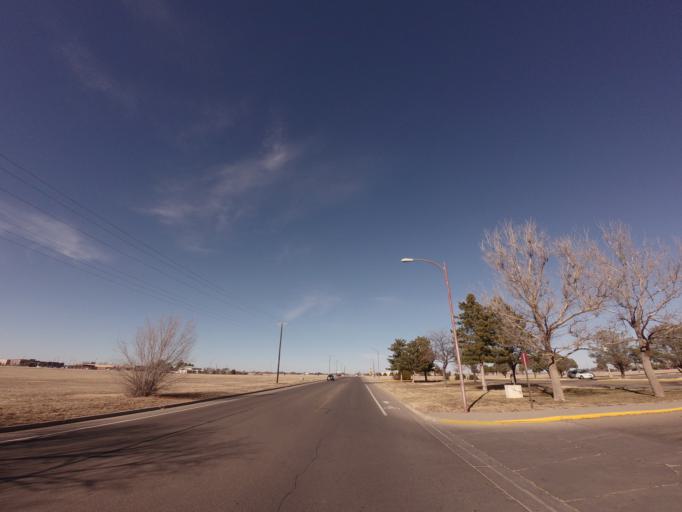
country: US
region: New Mexico
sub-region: Curry County
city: Clovis
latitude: 34.4028
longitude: -103.1682
